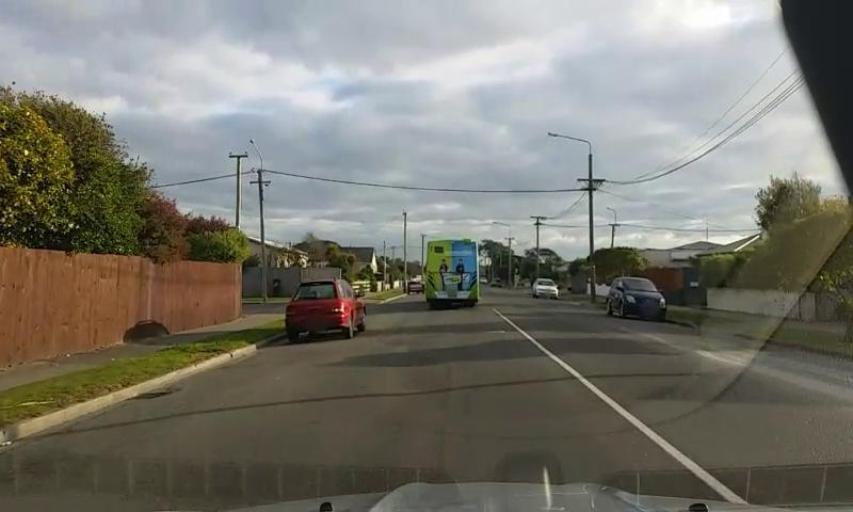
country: NZ
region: Canterbury
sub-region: Christchurch City
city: Christchurch
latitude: -43.5222
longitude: 172.7322
